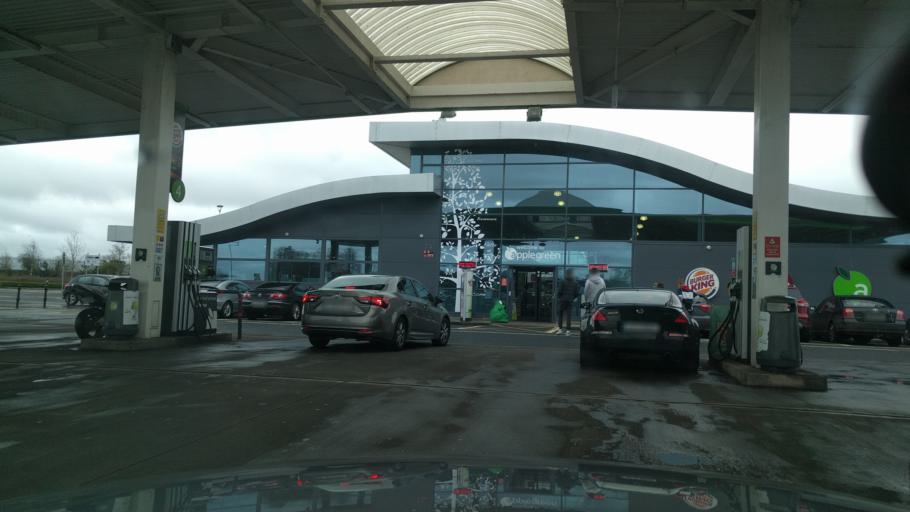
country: IE
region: Leinster
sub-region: An Mhi
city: Enfield
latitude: 53.4118
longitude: -6.8762
